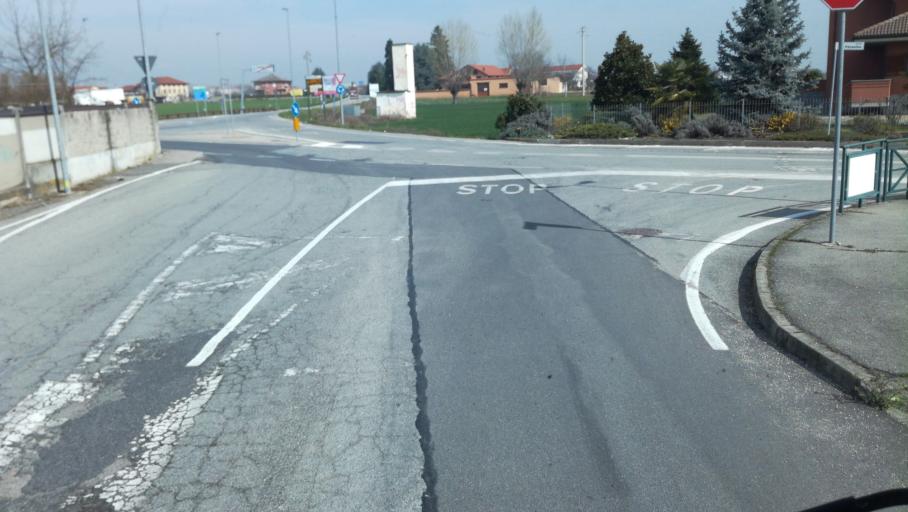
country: IT
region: Piedmont
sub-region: Provincia di Torino
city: Gerbole-Zucche
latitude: 44.9862
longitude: 7.5304
